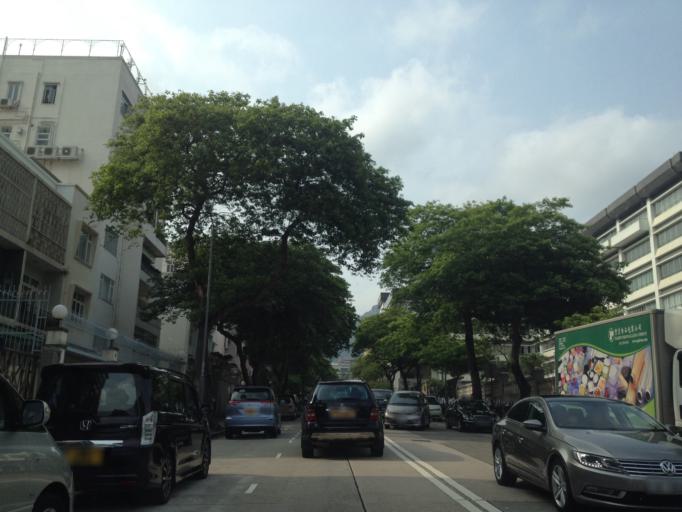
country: HK
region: Kowloon City
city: Kowloon
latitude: 22.3284
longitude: 114.1820
